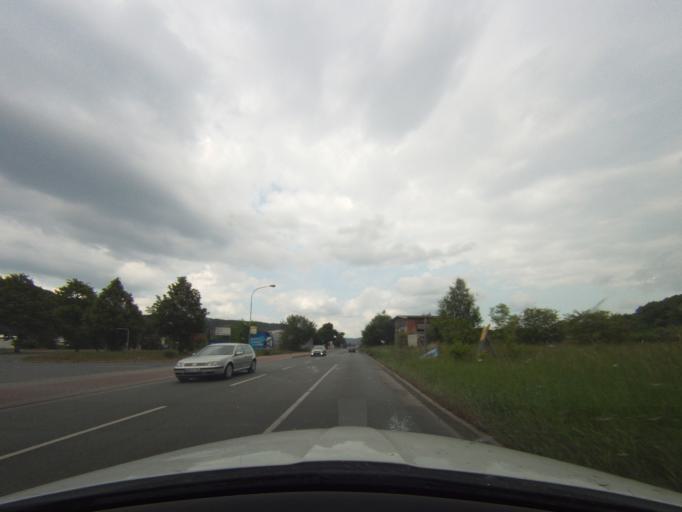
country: DE
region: Thuringia
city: Bad Blankenburg
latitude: 50.6836
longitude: 11.2800
